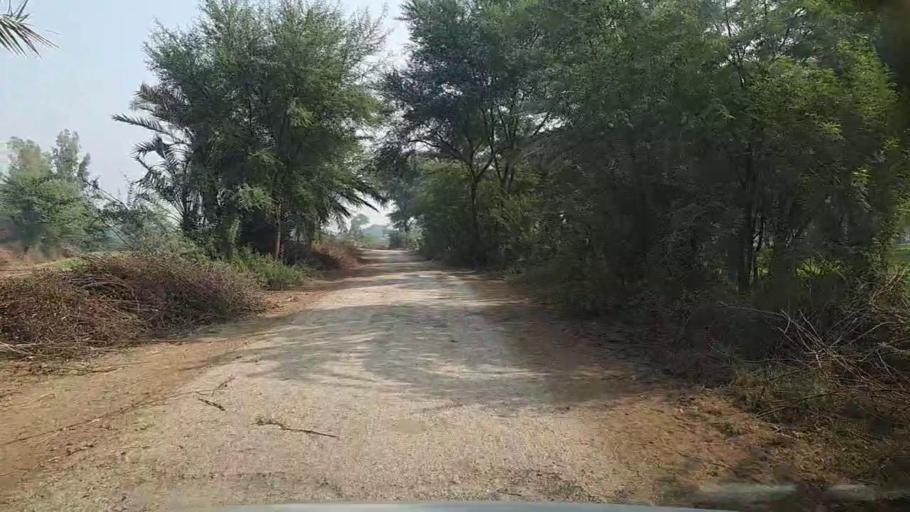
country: PK
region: Sindh
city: Setharja Old
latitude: 27.1385
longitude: 68.5079
